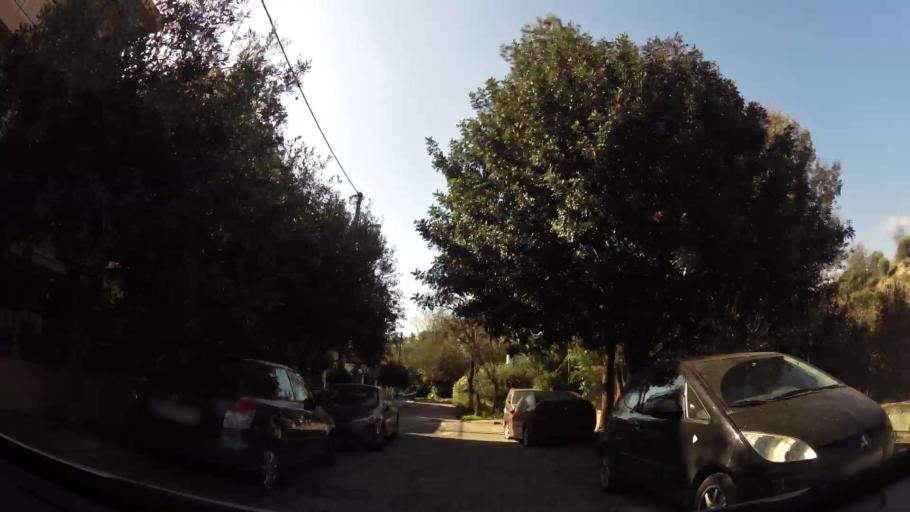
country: GR
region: Attica
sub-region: Nomarchia Athinas
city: Metamorfosi
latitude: 38.0687
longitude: 23.7536
